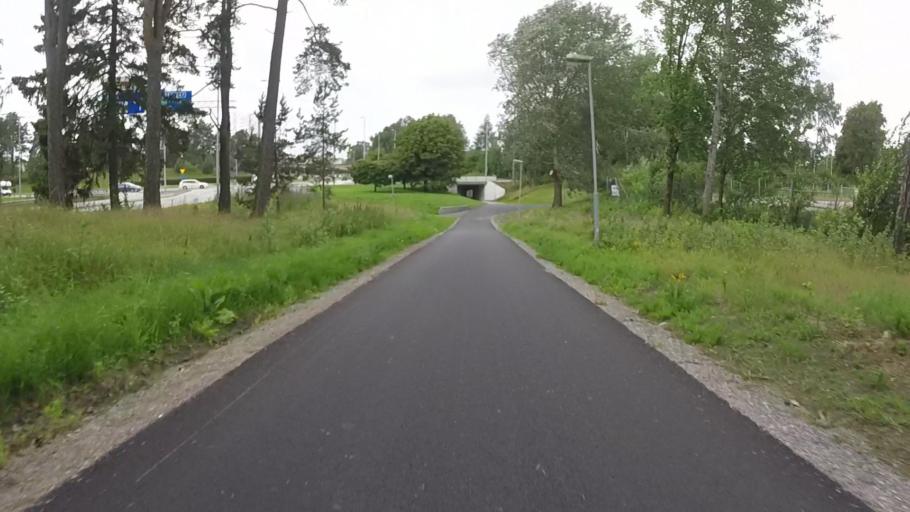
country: SE
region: Vaestra Goetaland
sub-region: Trollhattan
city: Trollhattan
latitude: 58.2797
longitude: 12.3074
